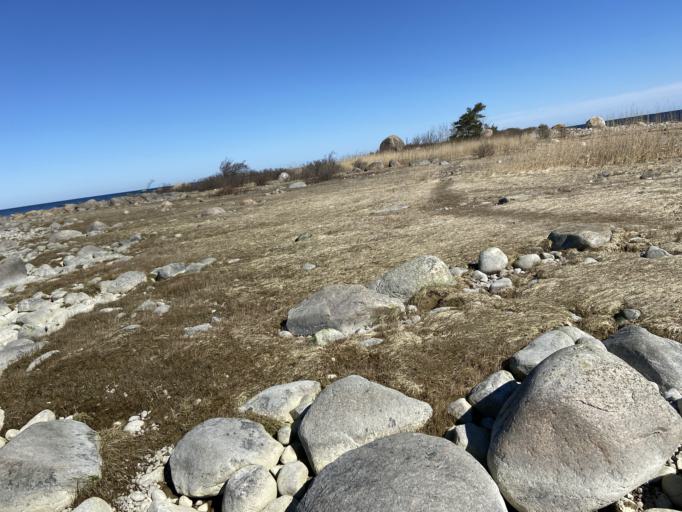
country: EE
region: Harju
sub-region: Loksa linn
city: Loksa
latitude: 59.6714
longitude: 25.6946
